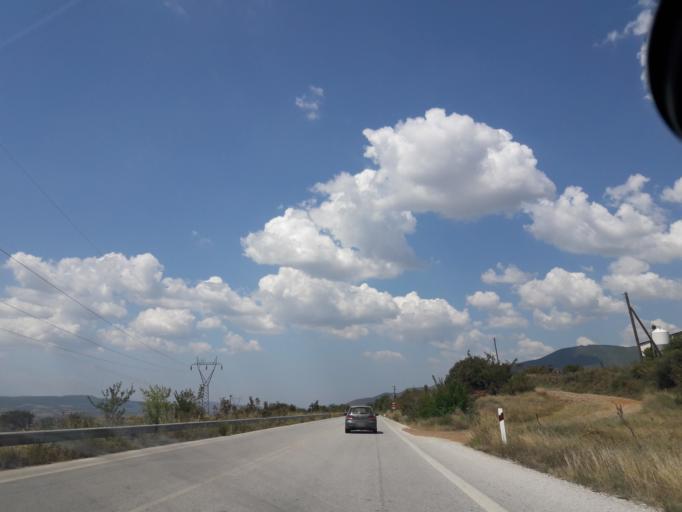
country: GR
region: Central Macedonia
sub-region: Nomos Chalkidikis
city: Galatista
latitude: 40.4607
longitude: 23.2844
